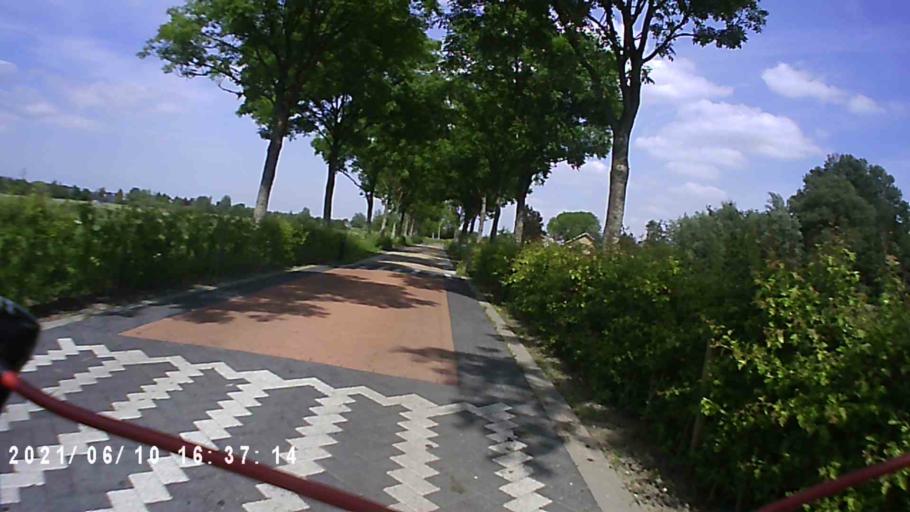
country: NL
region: Friesland
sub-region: Gemeente Achtkarspelen
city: Buitenpost
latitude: 53.2397
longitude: 6.1419
